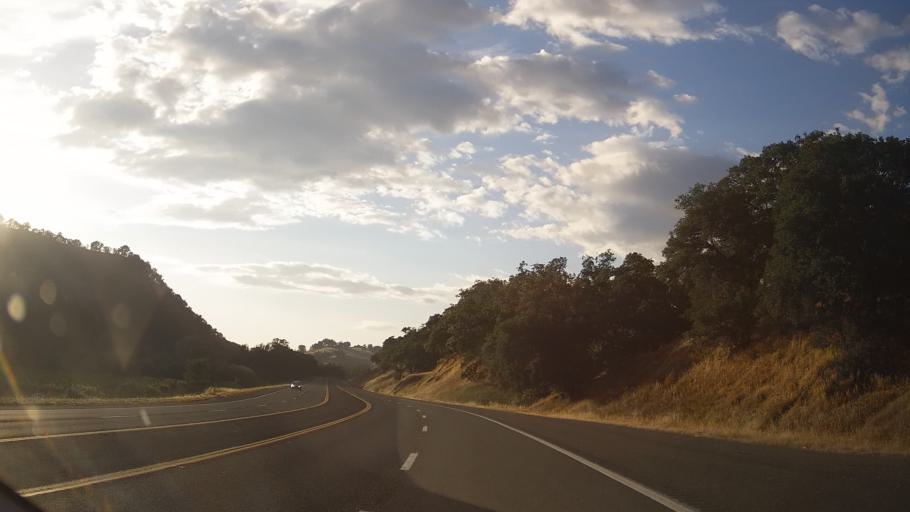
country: US
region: California
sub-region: Sonoma County
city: Cloverdale
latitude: 38.9285
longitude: -123.0570
